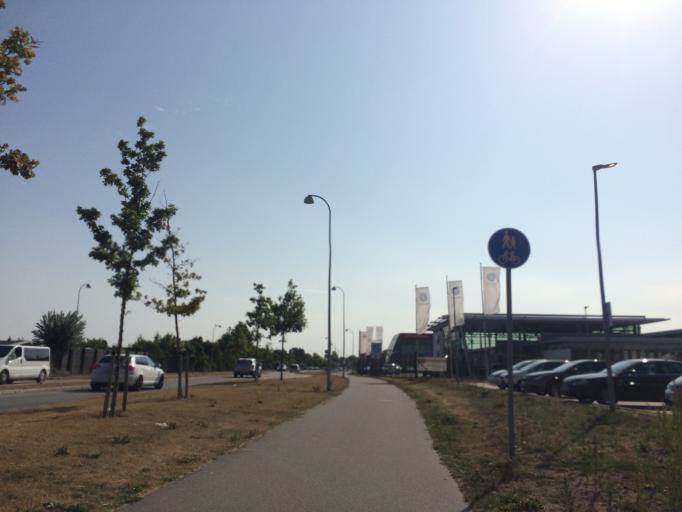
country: DK
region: Capital Region
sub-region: Ishoj Kommune
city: Ishoj
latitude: 55.6075
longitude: 12.3571
